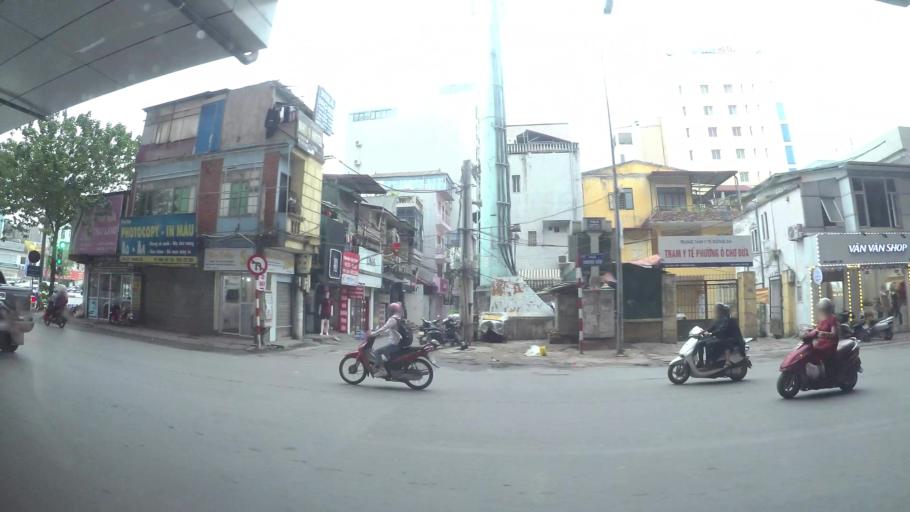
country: VN
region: Ha Noi
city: Dong Da
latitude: 21.0204
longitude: 105.8255
